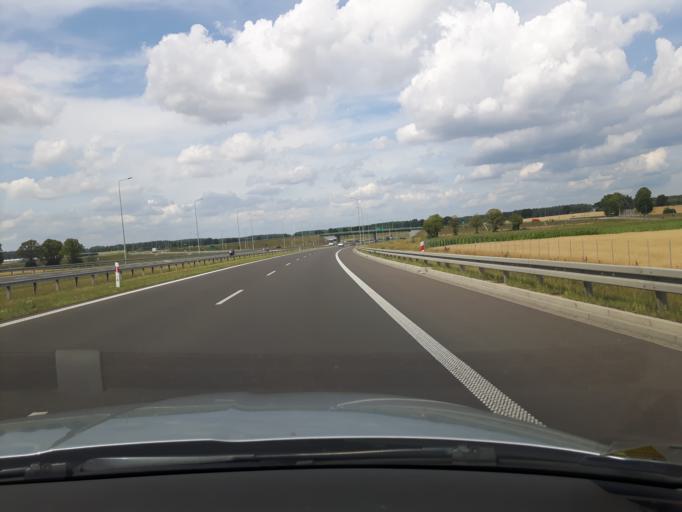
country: PL
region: Masovian Voivodeship
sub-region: Powiat mlawski
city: Wieczfnia Koscielna
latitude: 53.2244
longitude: 20.4209
